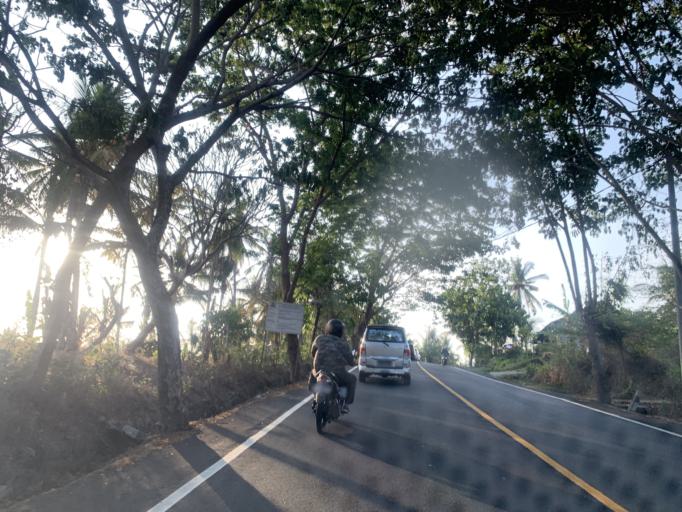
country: ID
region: Bali
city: Angkahgede
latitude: -8.4827
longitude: 114.9432
